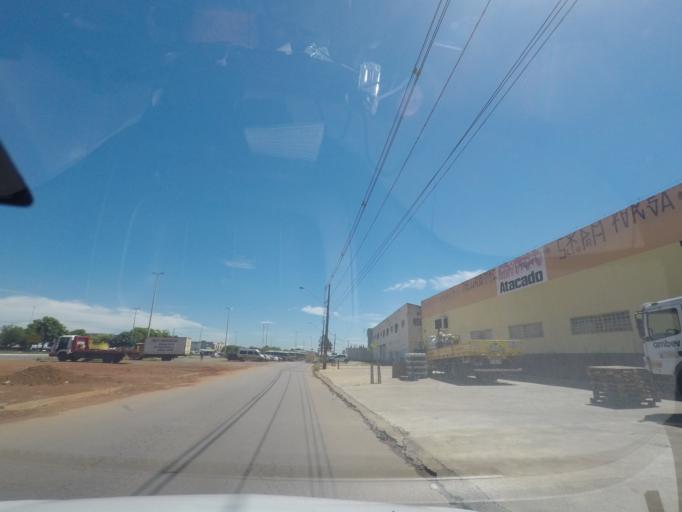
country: BR
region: Goias
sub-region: Aparecida De Goiania
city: Aparecida de Goiania
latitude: -16.7676
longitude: -49.3504
